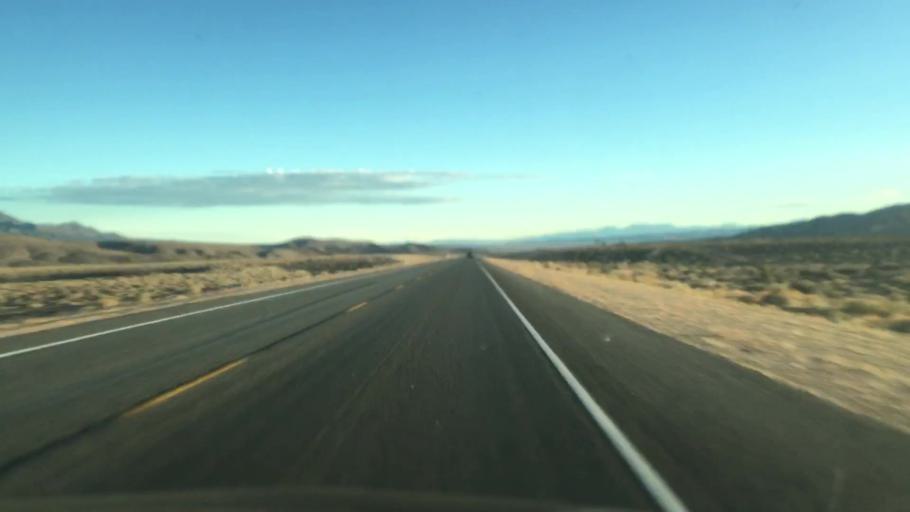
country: US
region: Nevada
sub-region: Esmeralda County
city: Goldfield
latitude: 37.5919
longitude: -117.2094
